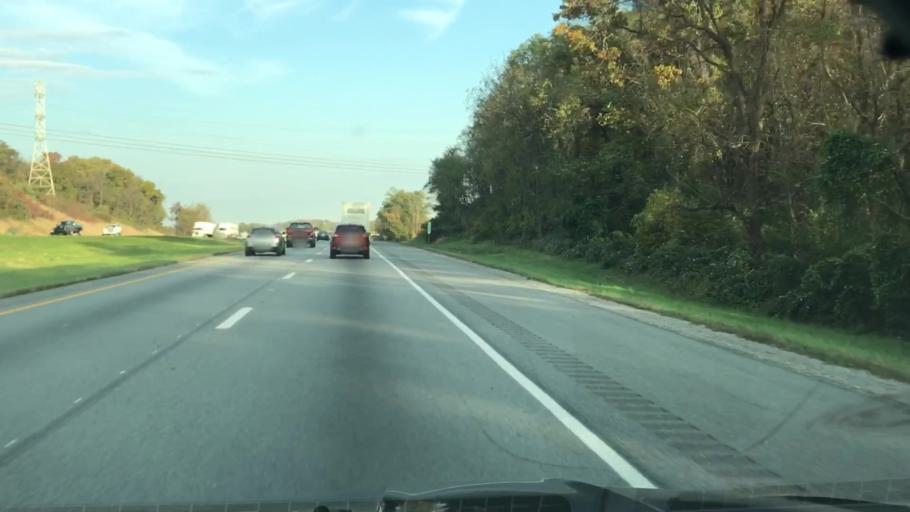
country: US
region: Pennsylvania
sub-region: Cumberland County
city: Schlusser
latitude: 40.2426
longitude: -77.1069
